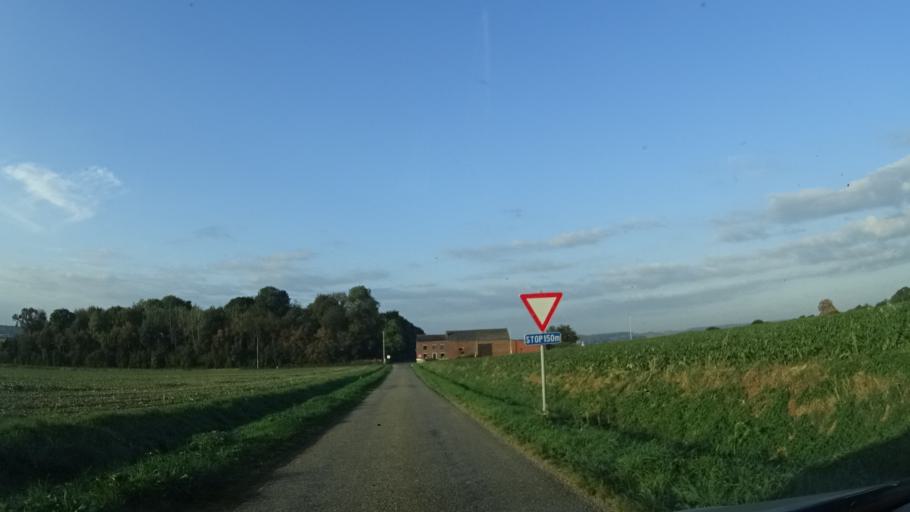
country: BE
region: Wallonia
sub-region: Province du Hainaut
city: Beaumont
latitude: 50.2320
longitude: 4.2719
